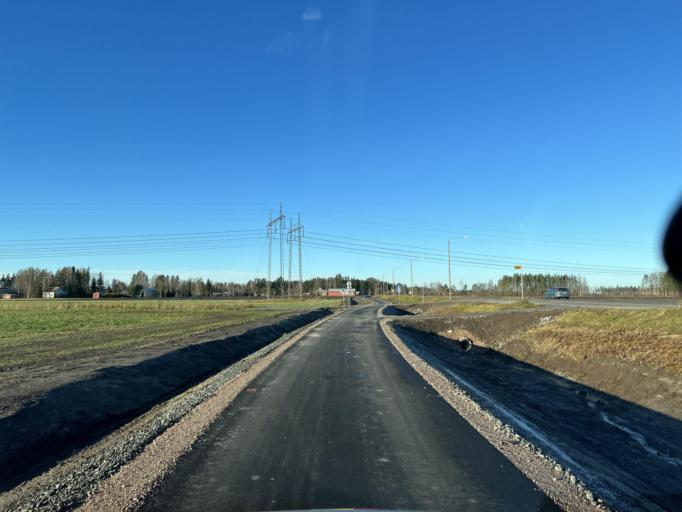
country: FI
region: Northern Ostrobothnia
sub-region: Nivala-Haapajaervi
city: Nivala
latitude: 63.9529
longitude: 24.8722
